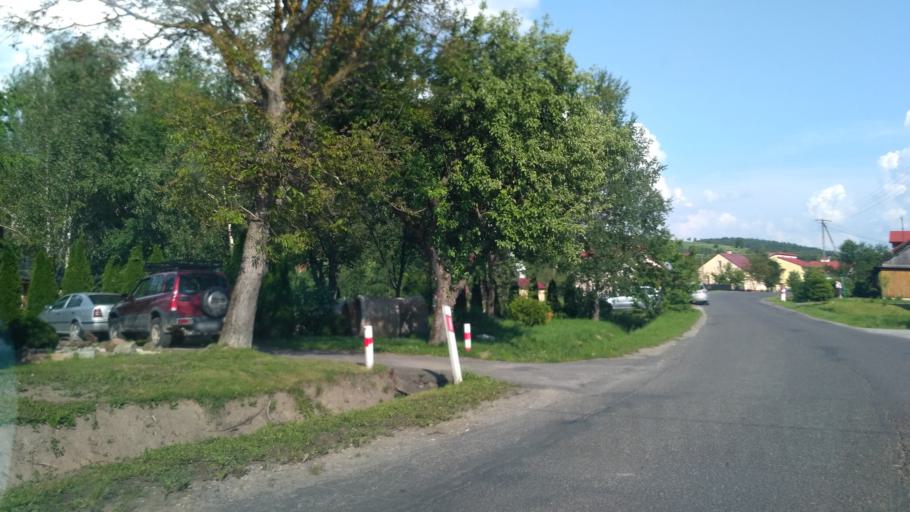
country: PL
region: Subcarpathian Voivodeship
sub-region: Powiat jaroslawski
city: Kramarzowka
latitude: 49.8765
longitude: 22.5046
